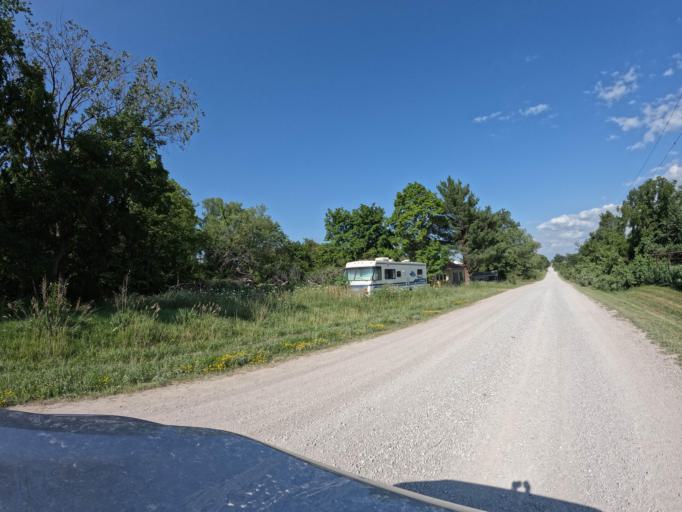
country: US
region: Iowa
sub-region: Appanoose County
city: Centerville
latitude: 40.7178
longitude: -93.0278
